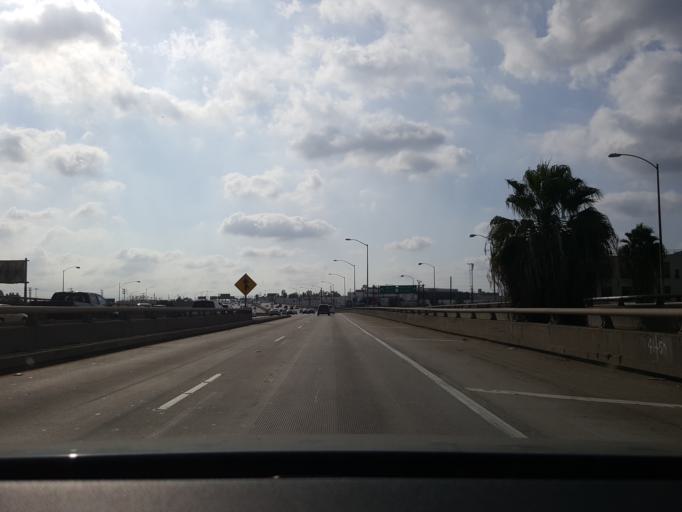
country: US
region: California
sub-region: Los Angeles County
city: Boyle Heights
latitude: 34.0291
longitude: -118.2279
